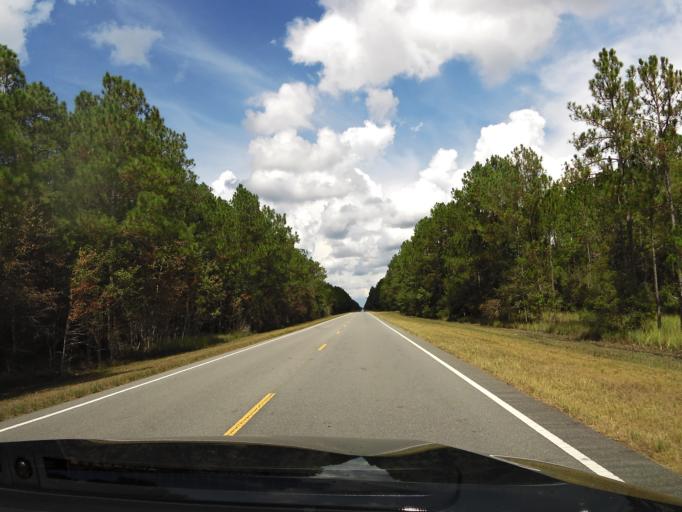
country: US
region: Georgia
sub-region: Charlton County
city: Folkston
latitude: 30.9460
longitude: -82.0228
